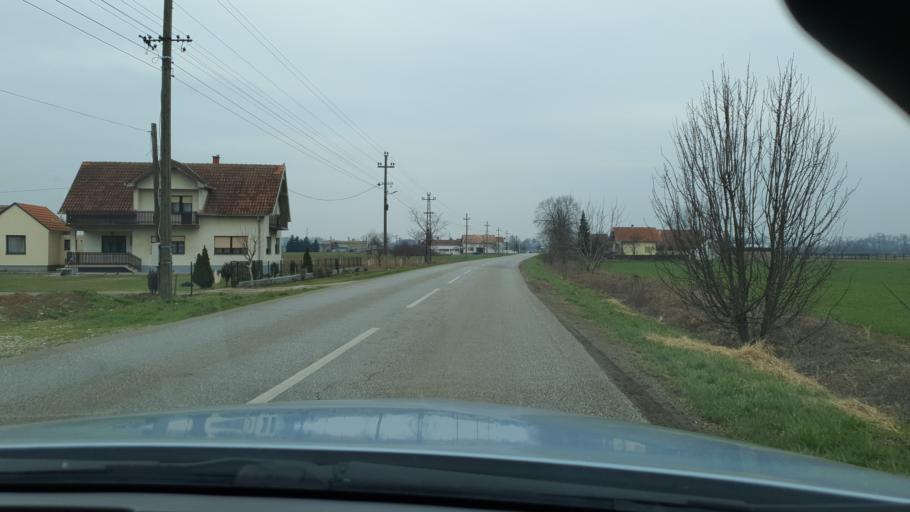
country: RS
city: Belotic
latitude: 44.8174
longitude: 19.5284
